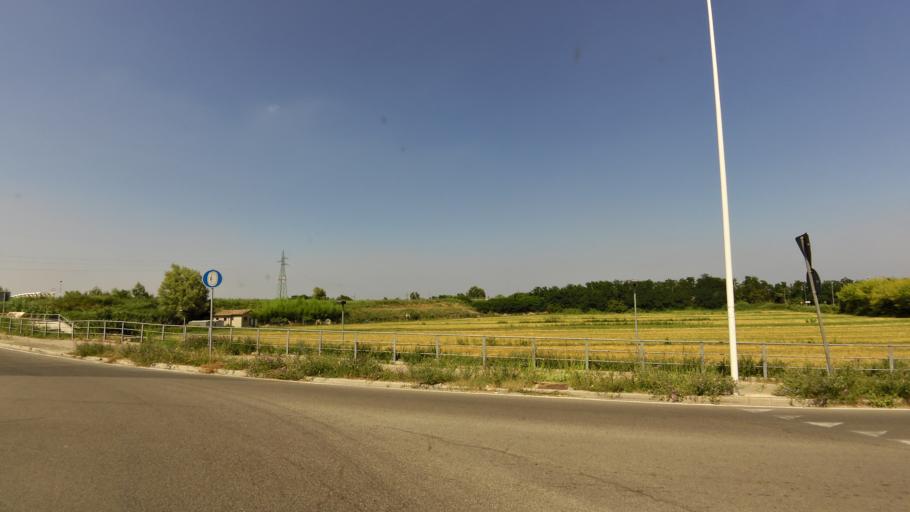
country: IT
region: Emilia-Romagna
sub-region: Provincia di Ravenna
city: Madonna Dell'Albero
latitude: 44.3961
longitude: 12.2156
